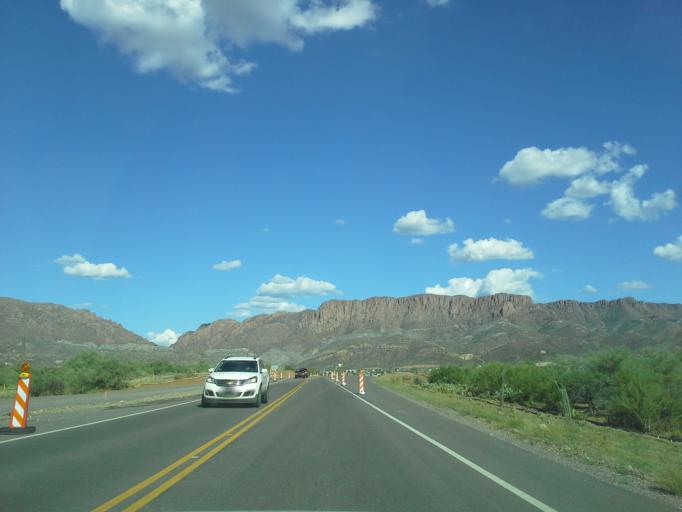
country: US
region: Arizona
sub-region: Pinal County
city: Superior
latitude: 33.2841
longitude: -111.1285
